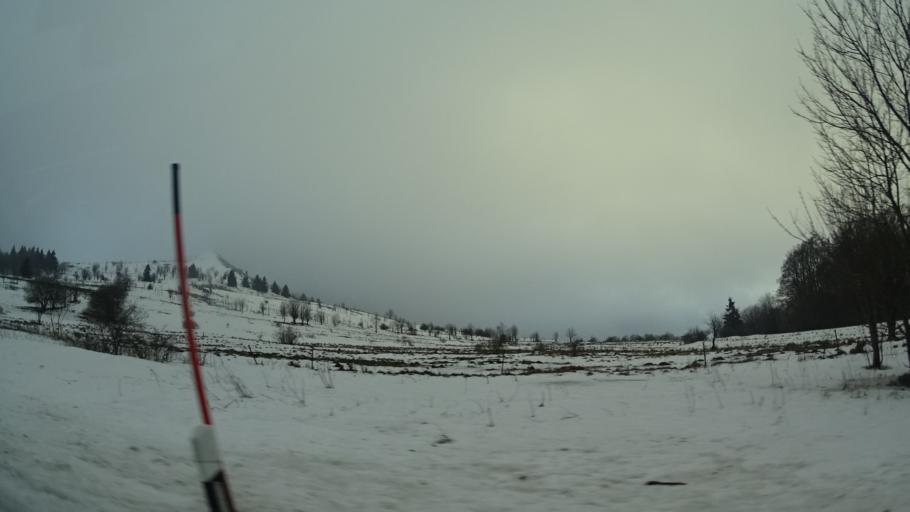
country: DE
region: Hesse
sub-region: Regierungsbezirk Kassel
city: Gersfeld
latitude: 50.5087
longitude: 9.9396
